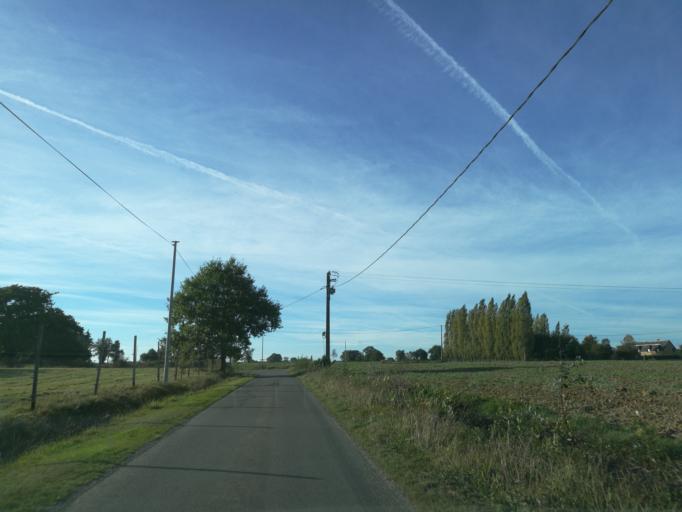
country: FR
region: Brittany
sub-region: Departement d'Ille-et-Vilaine
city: Bedee
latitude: 48.1982
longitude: -1.9535
